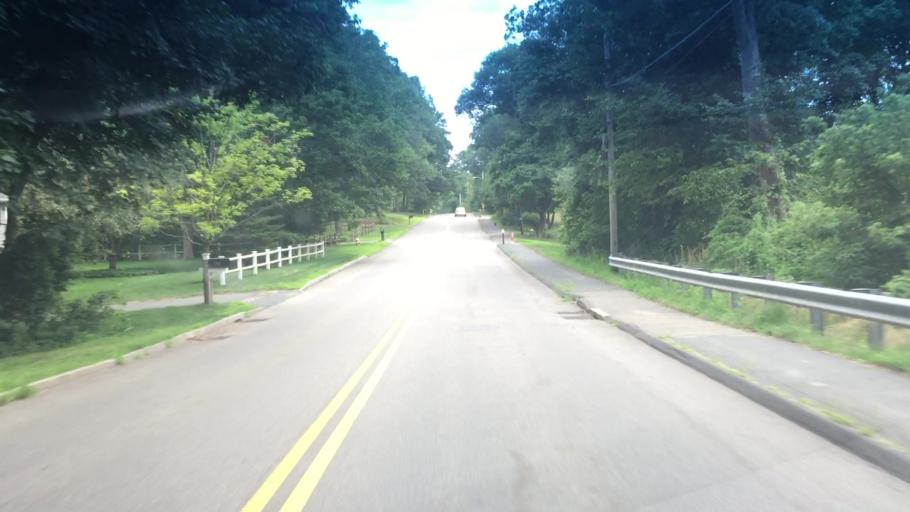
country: US
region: Massachusetts
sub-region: Norfolk County
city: Medway
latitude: 42.1252
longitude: -71.3986
